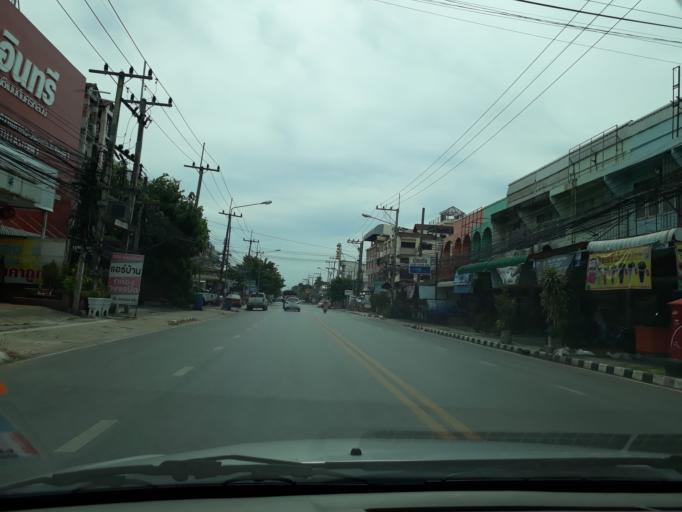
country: TH
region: Khon Kaen
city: Khon Kaen
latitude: 16.4360
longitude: 102.8507
